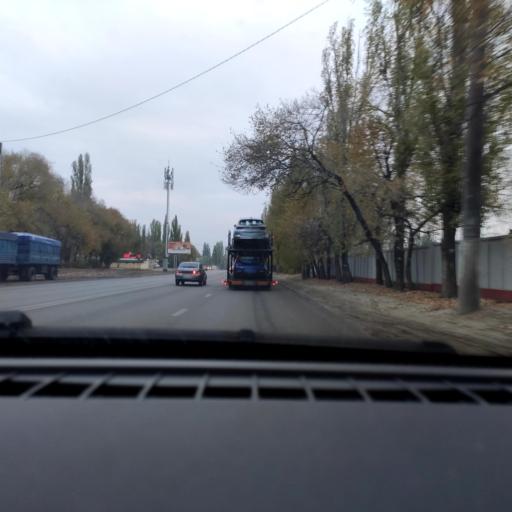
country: RU
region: Voronezj
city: Voronezh
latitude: 51.6400
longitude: 39.2651
